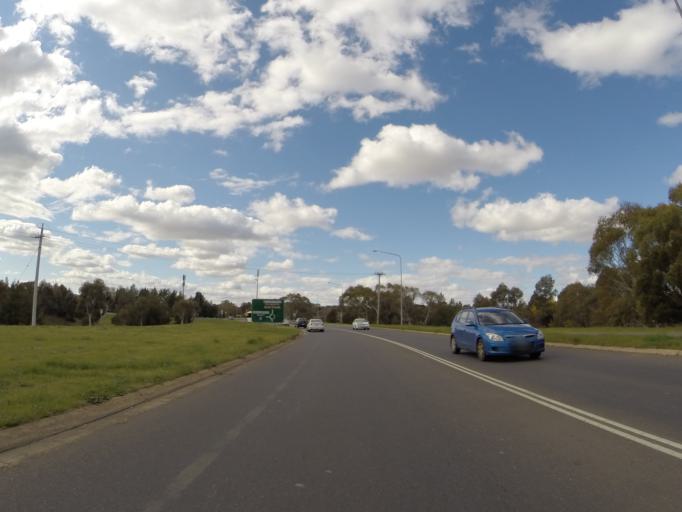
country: AU
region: Australian Capital Territory
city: Belconnen
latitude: -35.2150
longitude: 149.0859
